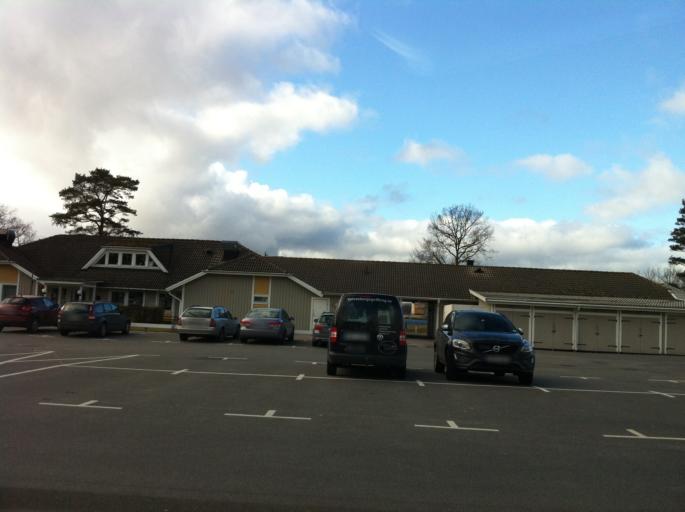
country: SE
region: Skane
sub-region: Bromolla Kommun
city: Bromoella
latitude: 56.0619
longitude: 14.4835
